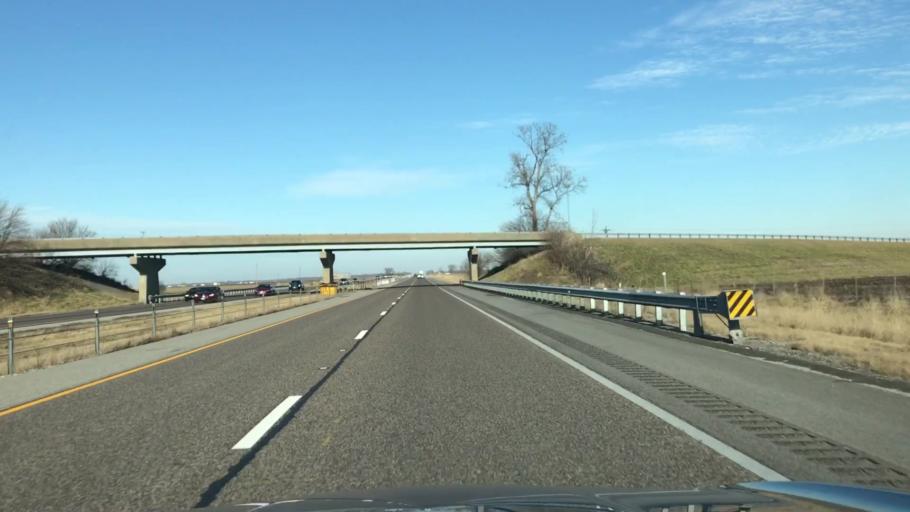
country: US
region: Illinois
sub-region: Madison County
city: Edwardsville
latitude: 38.8306
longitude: -89.8790
